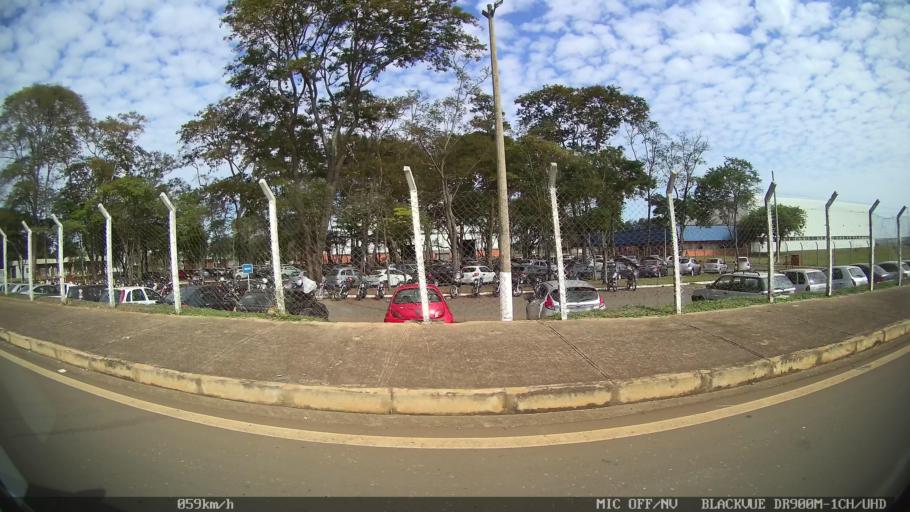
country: BR
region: Sao Paulo
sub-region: Santa Barbara D'Oeste
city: Santa Barbara d'Oeste
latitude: -22.7621
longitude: -47.4584
